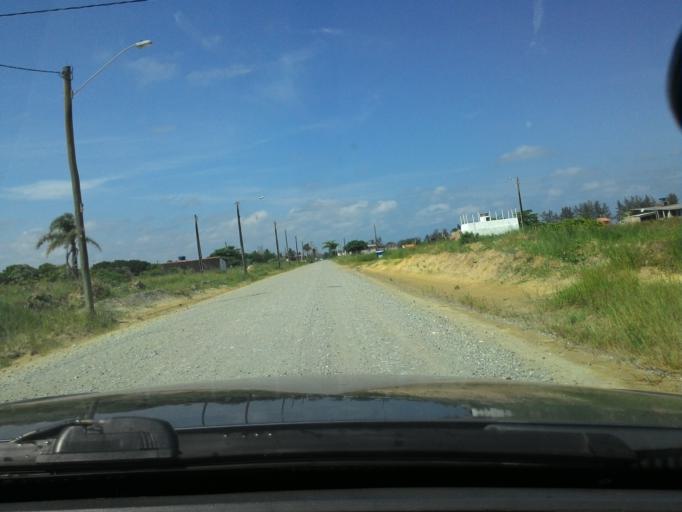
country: BR
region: Sao Paulo
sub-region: Iguape
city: Iguape
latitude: -24.8496
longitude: -47.6982
